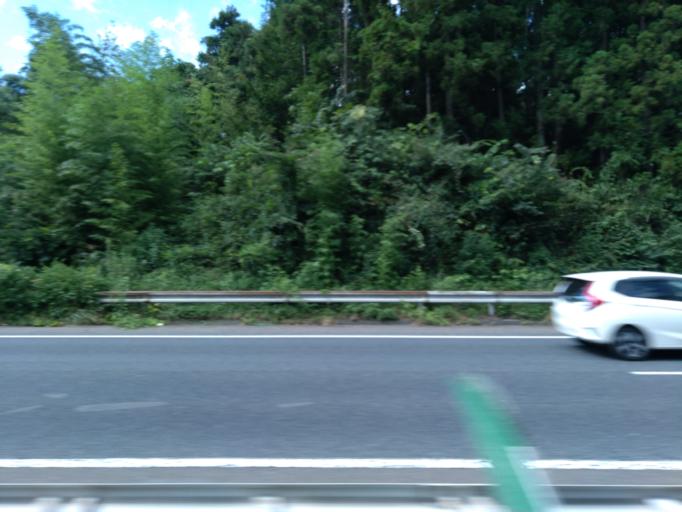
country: JP
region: Miyagi
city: Tomiya
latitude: 38.4481
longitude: 140.9126
